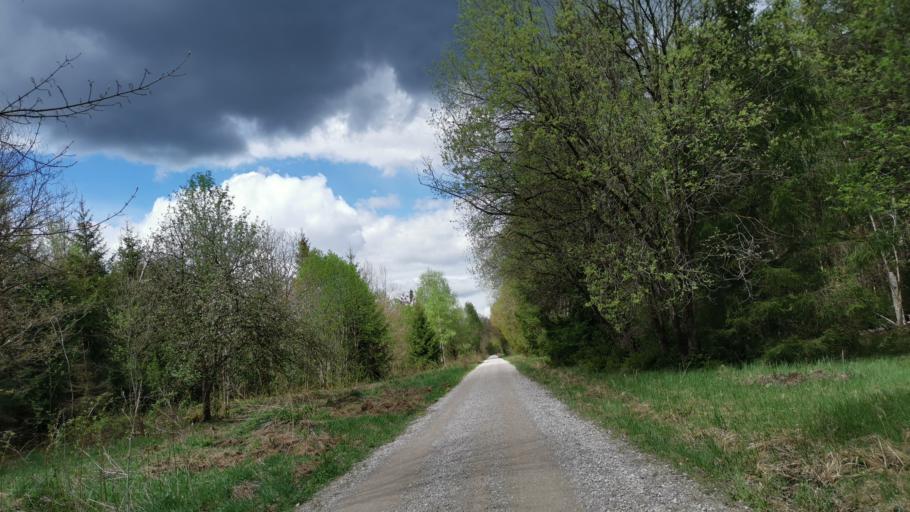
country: DE
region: Bavaria
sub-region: Upper Bavaria
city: Neuried
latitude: 48.0633
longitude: 11.4426
